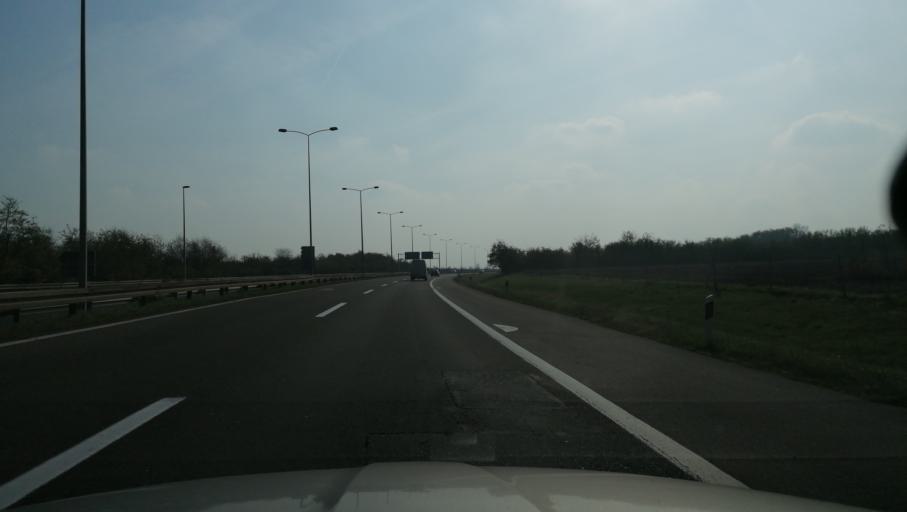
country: RS
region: Central Serbia
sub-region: Podunavski Okrug
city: Smederevo
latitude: 44.5769
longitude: 20.9795
